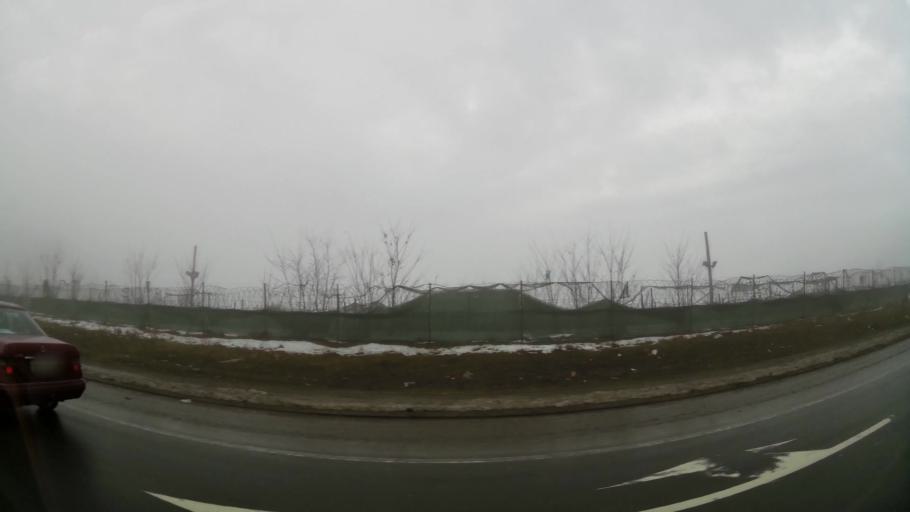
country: XK
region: Pristina
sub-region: Komuna e Prishtines
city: Pristina
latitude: 42.6570
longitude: 21.1380
